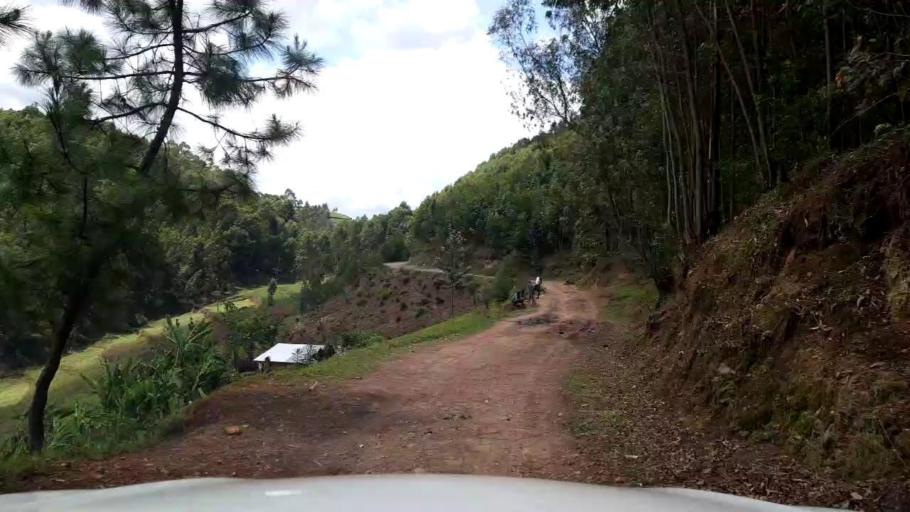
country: RW
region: Northern Province
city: Byumba
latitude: -1.5232
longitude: 30.1304
